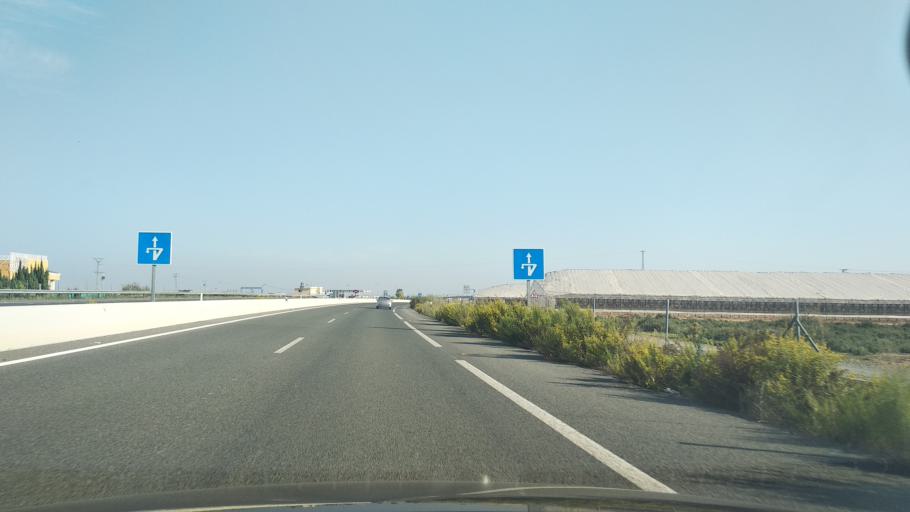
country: ES
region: Murcia
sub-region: Murcia
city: San Javier
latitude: 37.8548
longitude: -0.8835
